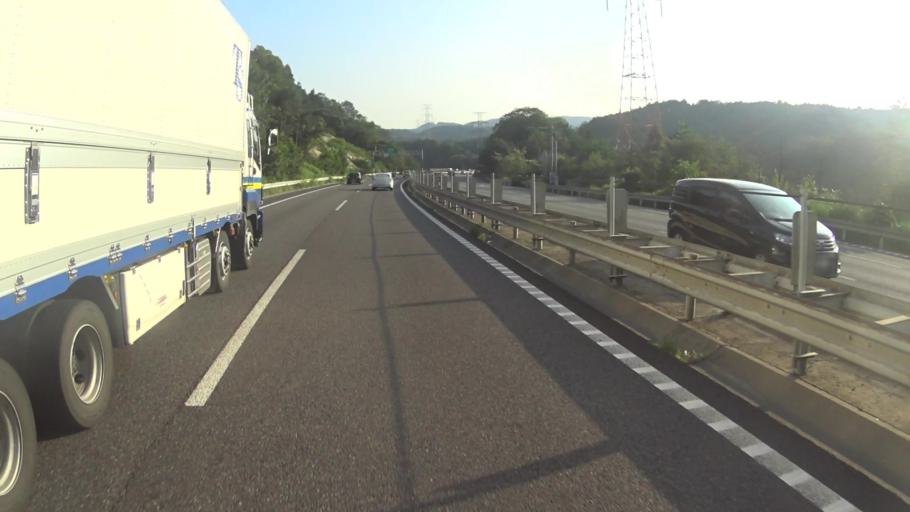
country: JP
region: Shiga Prefecture
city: Otsu-shi
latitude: 34.9247
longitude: 135.8874
